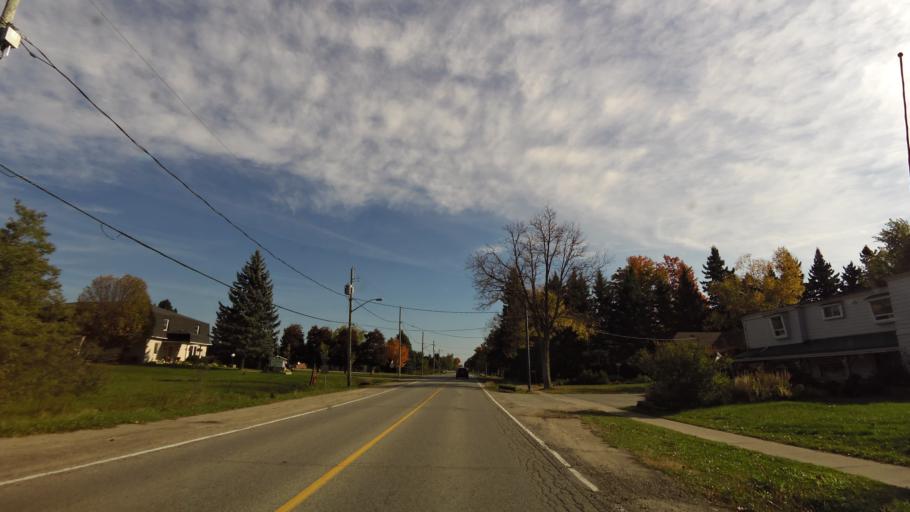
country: CA
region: Ontario
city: Orangeville
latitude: 43.7653
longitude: -80.0573
